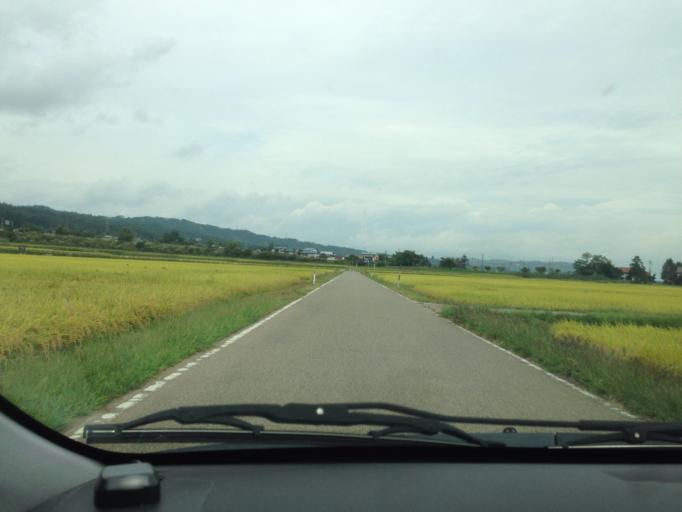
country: JP
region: Fukushima
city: Kitakata
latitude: 37.5673
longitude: 139.8045
